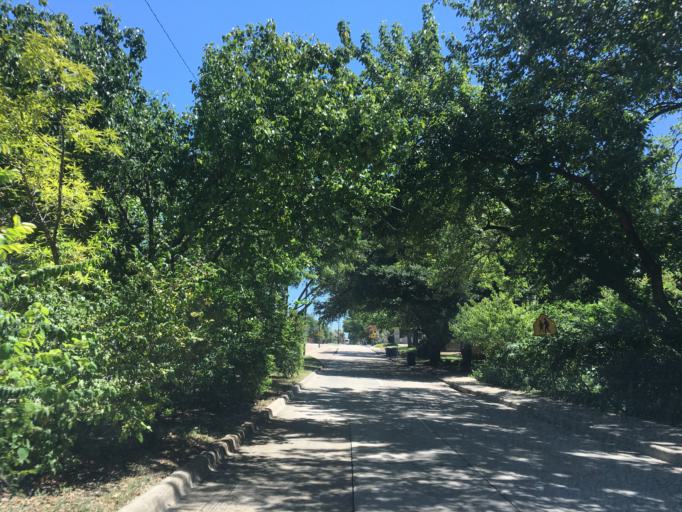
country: US
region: Texas
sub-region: Dallas County
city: Highland Park
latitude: 32.8488
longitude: -96.7090
